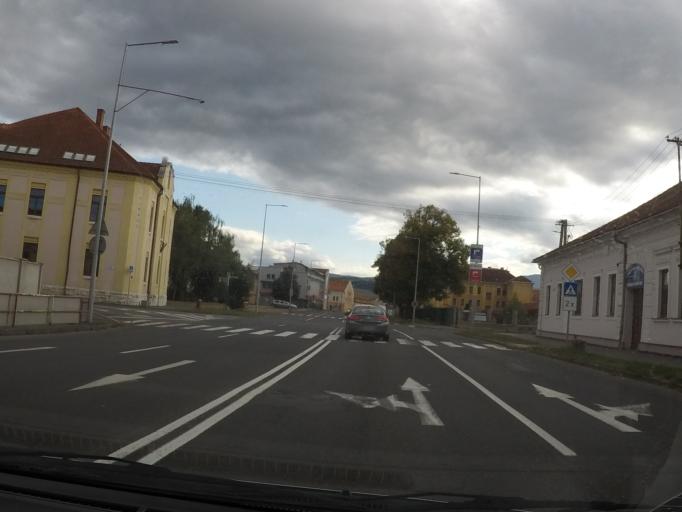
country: SK
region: Kosicky
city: Spisska Nova Ves
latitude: 48.9476
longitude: 20.5652
